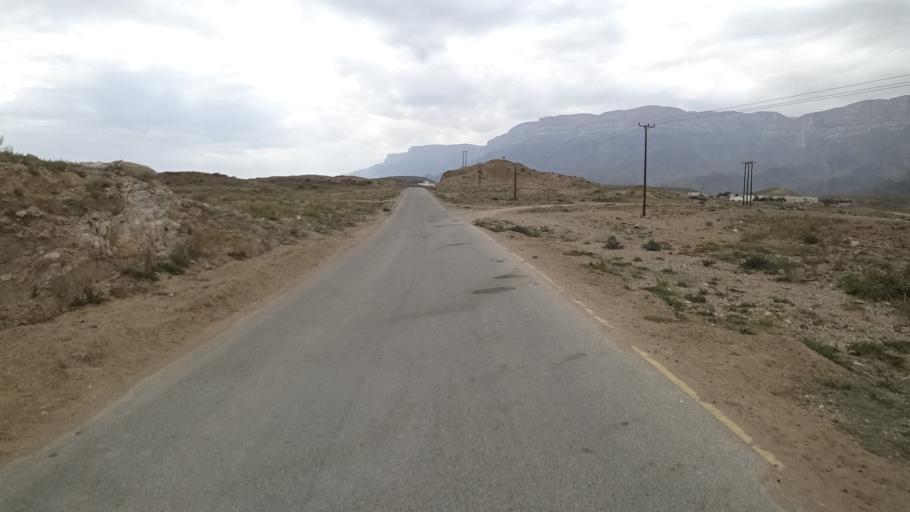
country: OM
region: Zufar
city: Salalah
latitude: 17.1622
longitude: 54.9882
